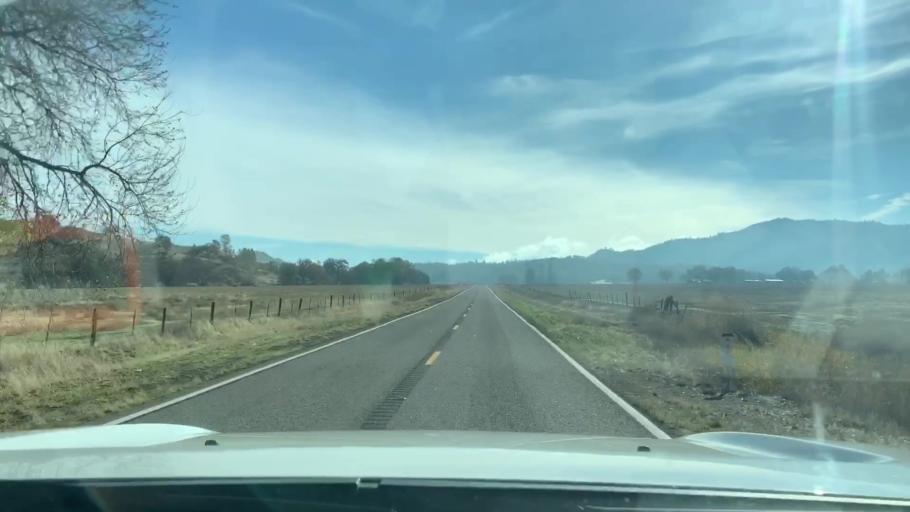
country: US
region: California
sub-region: Fresno County
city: Coalinga
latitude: 36.1818
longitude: -120.6974
